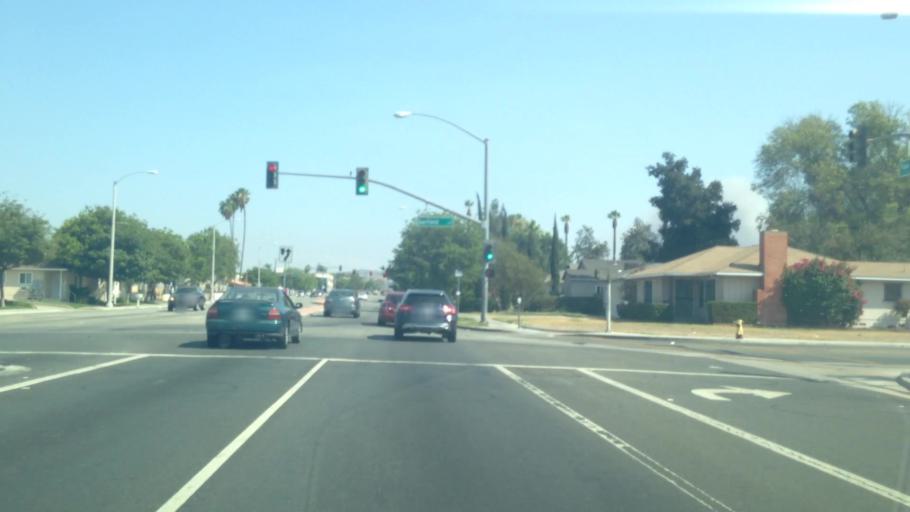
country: US
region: California
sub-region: Riverside County
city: Pedley
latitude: 33.9237
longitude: -117.4494
